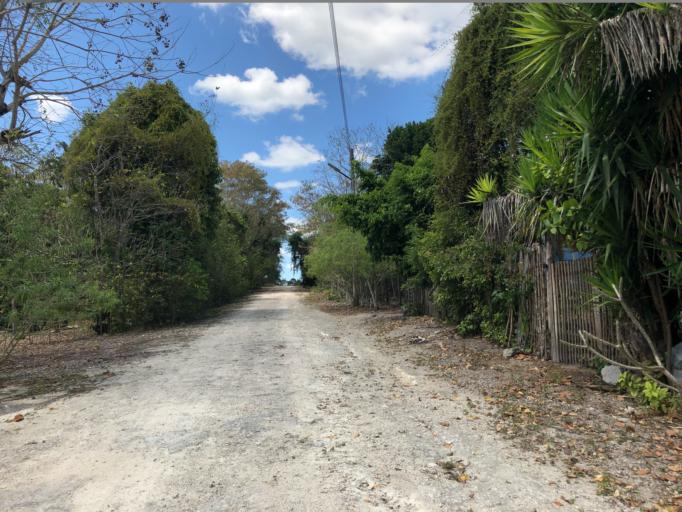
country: MX
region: Quintana Roo
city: Nicolas Bravo
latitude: 18.4494
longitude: -89.3075
